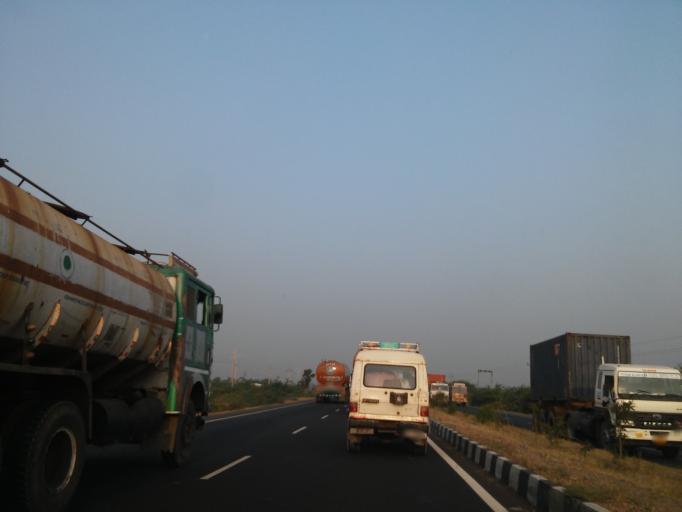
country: IN
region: Gujarat
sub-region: Kachchh
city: Bhachau
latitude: 23.2934
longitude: 70.5729
